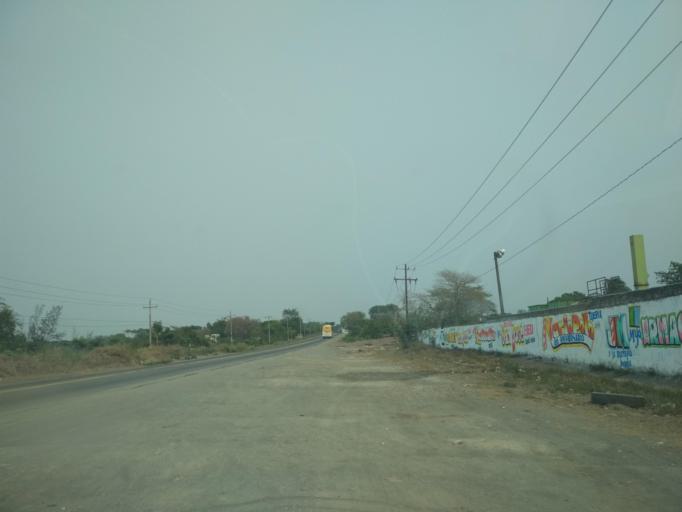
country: MX
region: Veracruz
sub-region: Veracruz
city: Delfino Victoria (Santa Fe)
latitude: 19.1870
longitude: -96.2741
